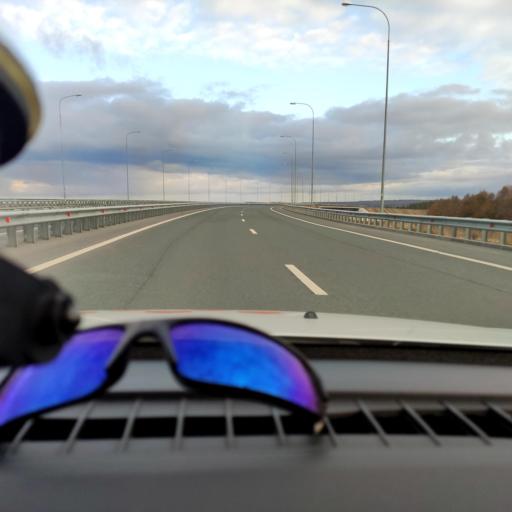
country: RU
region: Samara
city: Bereza
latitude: 53.4977
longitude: 50.1168
